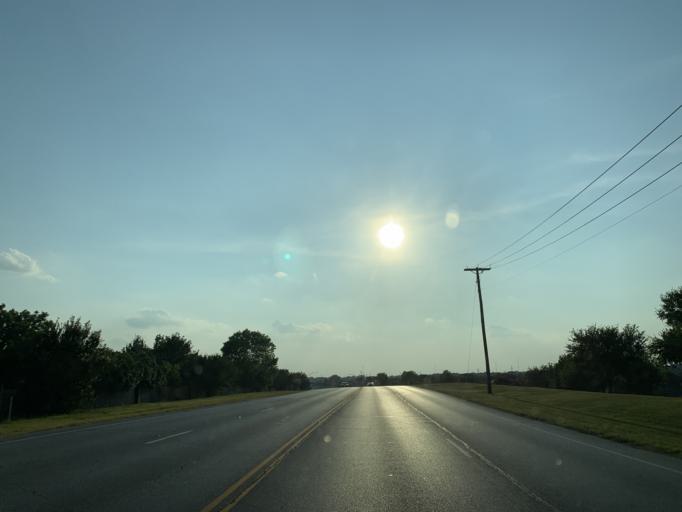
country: US
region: Texas
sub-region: Tarrant County
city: Hurst
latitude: 32.8025
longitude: -97.1920
